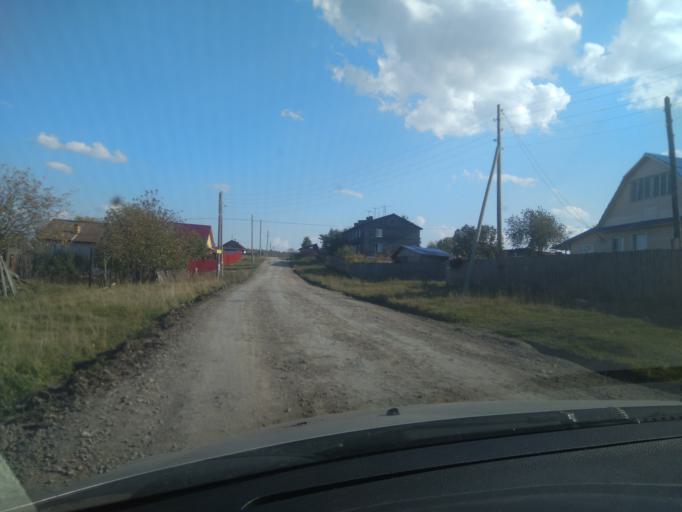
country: RU
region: Sverdlovsk
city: Pokrovskoye
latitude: 56.4356
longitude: 61.5884
